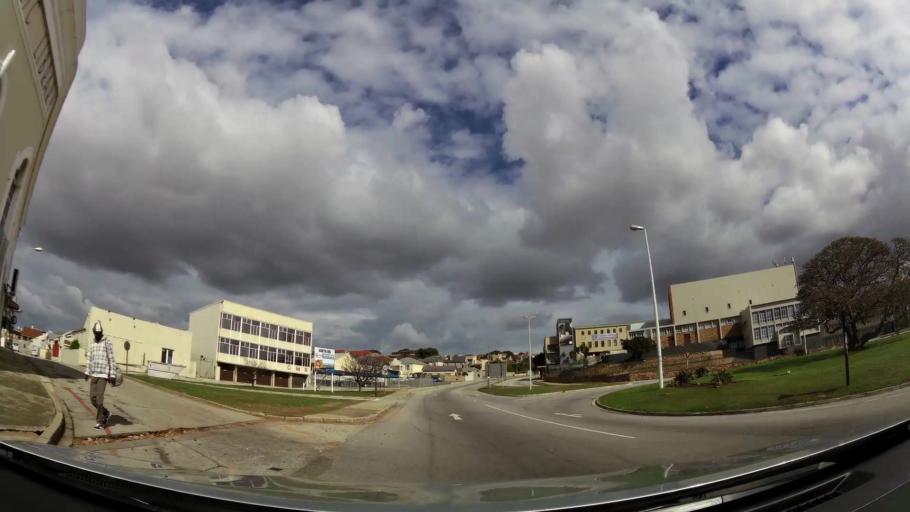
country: ZA
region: Eastern Cape
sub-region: Nelson Mandela Bay Metropolitan Municipality
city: Port Elizabeth
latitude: -33.9474
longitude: 25.6032
